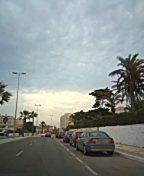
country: ES
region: Murcia
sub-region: Murcia
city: La Manga del Mar Menor
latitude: 37.7097
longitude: -0.7423
